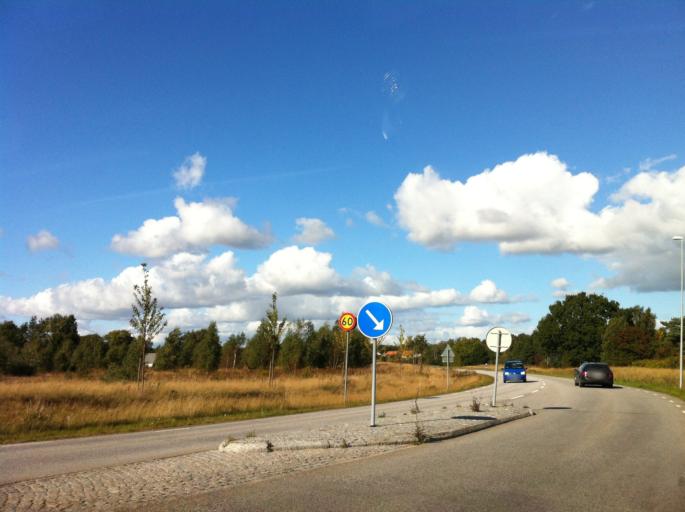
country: SE
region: Skane
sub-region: Sjobo Kommun
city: Sjoebo
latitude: 55.6330
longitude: 13.7333
